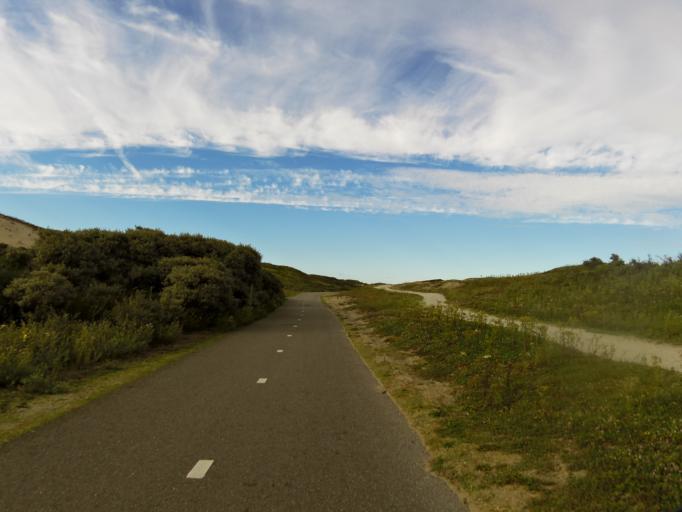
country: NL
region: South Holland
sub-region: Gemeente Katwijk
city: Katwijk aan Zee
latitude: 52.1778
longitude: 4.3699
